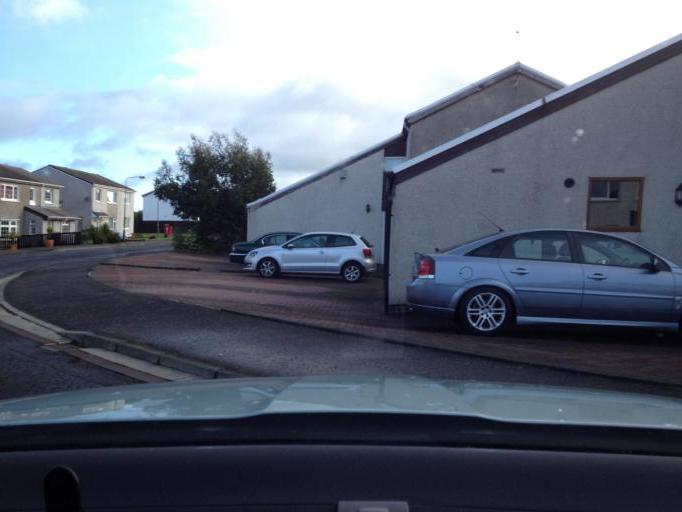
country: GB
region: Scotland
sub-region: West Lothian
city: East Calder
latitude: 55.8889
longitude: -3.4595
